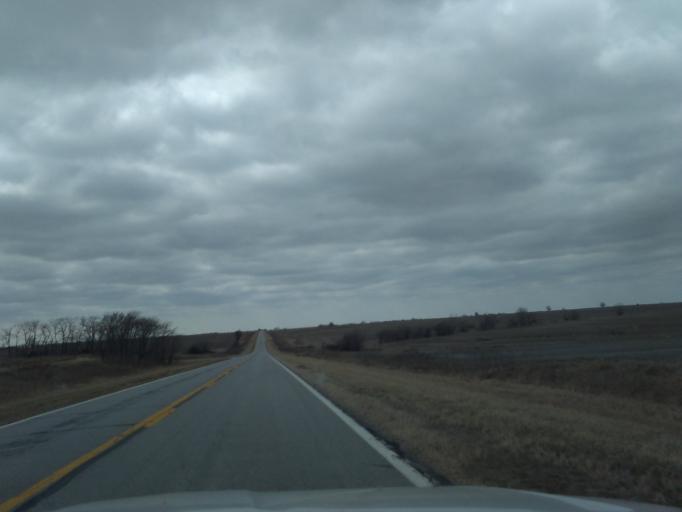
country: US
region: Nebraska
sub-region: Pawnee County
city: Pawnee City
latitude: 40.0447
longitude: -96.3865
